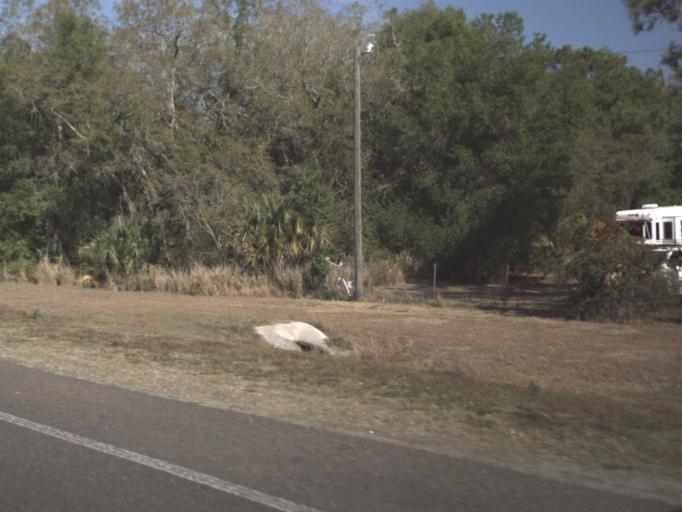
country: US
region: Florida
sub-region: Lake County
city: Howie In The Hills
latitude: 28.6408
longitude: -81.7969
